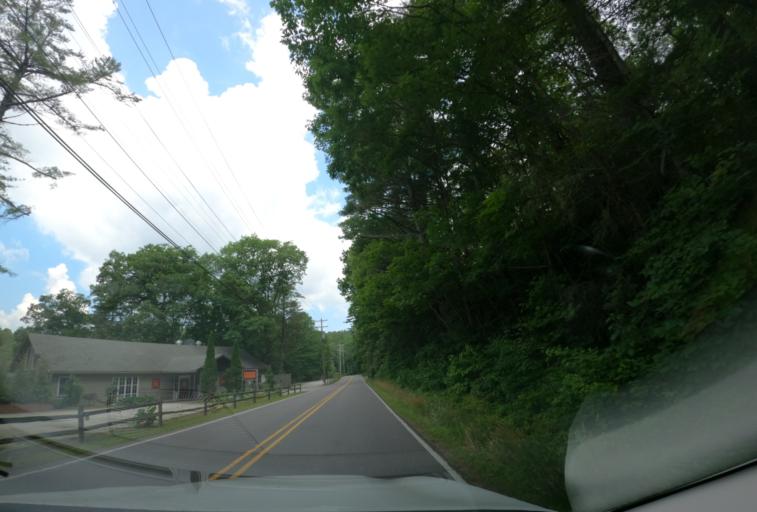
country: US
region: North Carolina
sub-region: Macon County
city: Franklin
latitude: 35.0630
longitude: -83.2195
